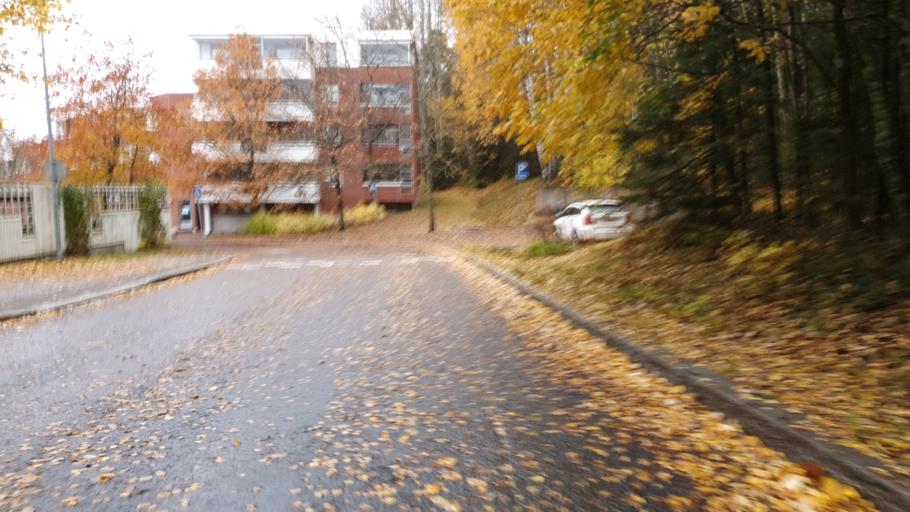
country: FI
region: Uusimaa
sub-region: Helsinki
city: Teekkarikylae
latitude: 60.2498
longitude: 24.8567
